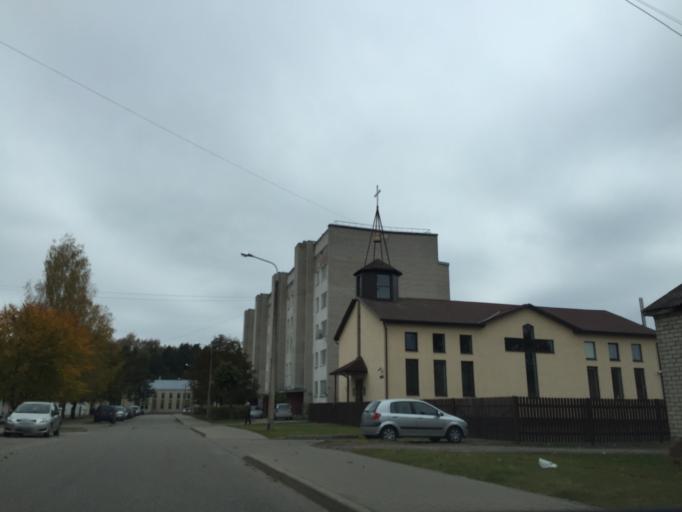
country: LV
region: Olaine
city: Olaine
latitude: 56.7873
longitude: 23.9362
